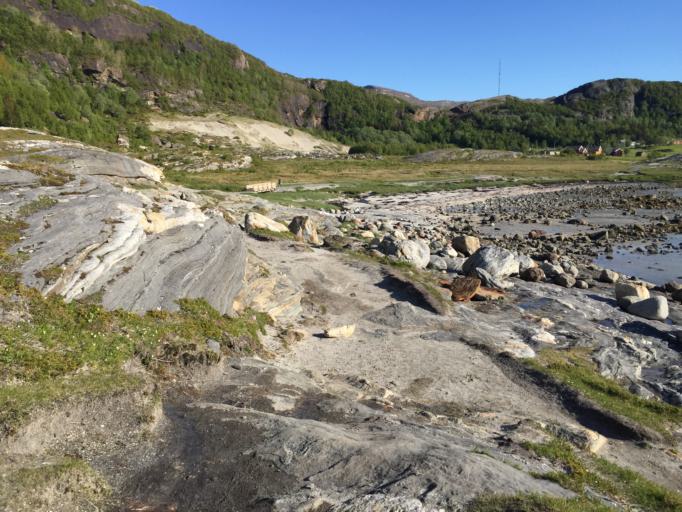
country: NO
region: Nordland
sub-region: Bodo
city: Loding
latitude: 67.4144
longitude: 14.6328
